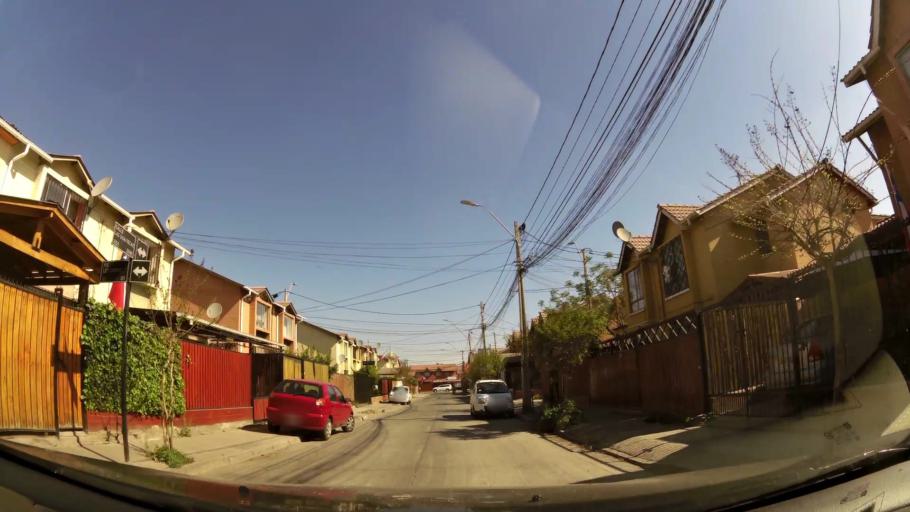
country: CL
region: Santiago Metropolitan
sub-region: Provincia de Maipo
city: San Bernardo
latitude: -33.6151
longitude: -70.7058
